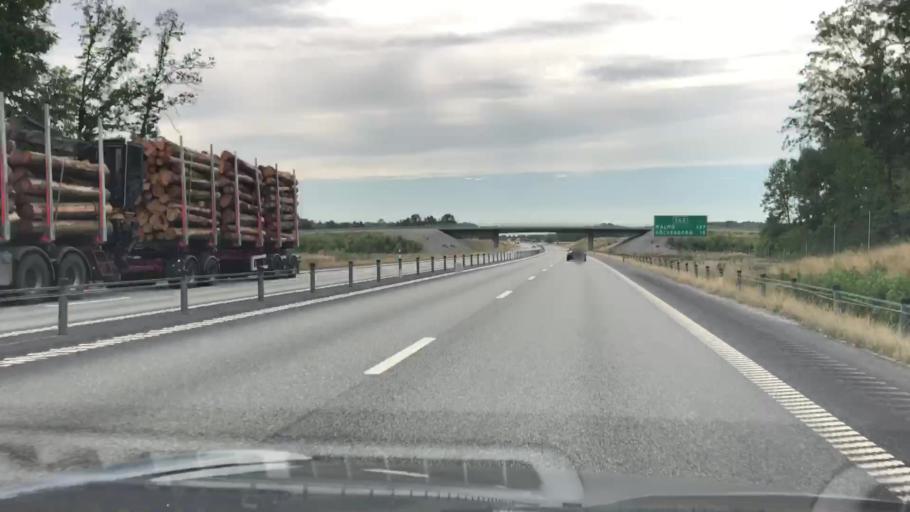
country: SE
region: Blekinge
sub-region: Karlshamns Kommun
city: Morrum
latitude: 56.1584
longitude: 14.6668
